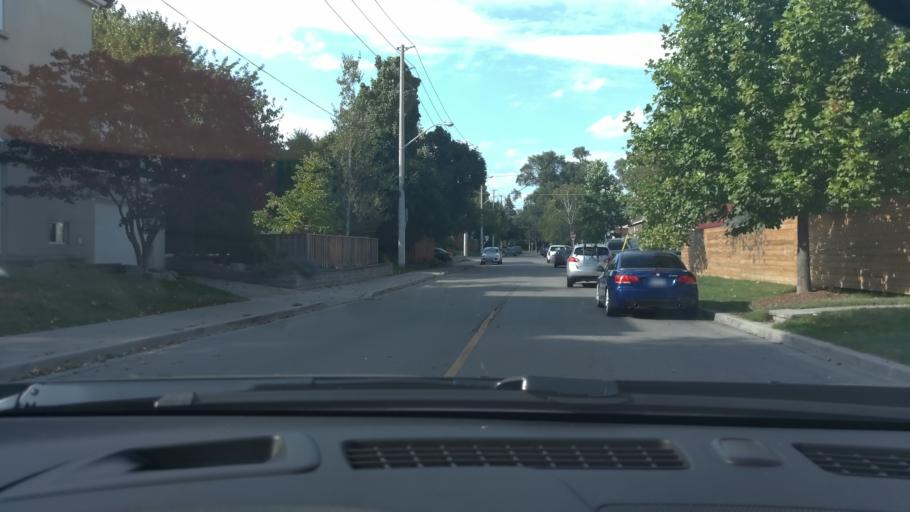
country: CA
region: Ontario
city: Toronto
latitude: 43.7150
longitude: -79.3626
